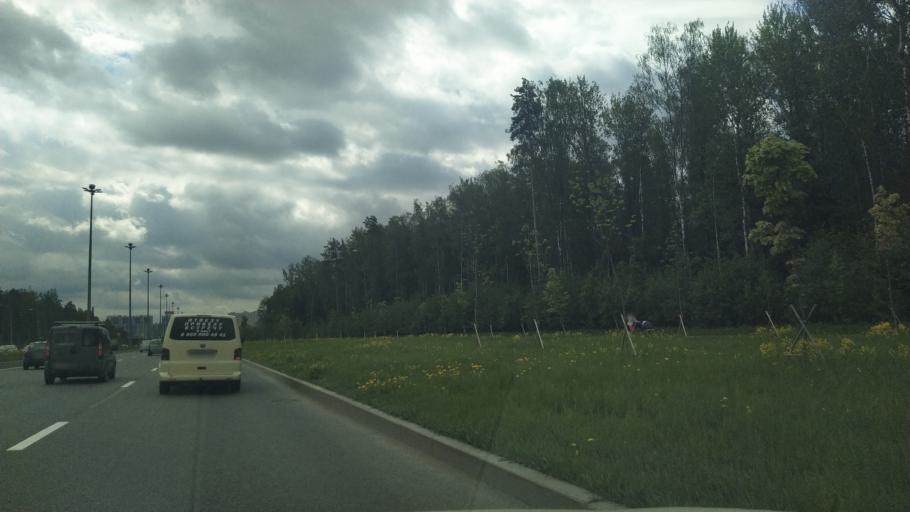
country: RU
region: Leningrad
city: Untolovo
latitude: 60.0505
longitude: 30.2293
